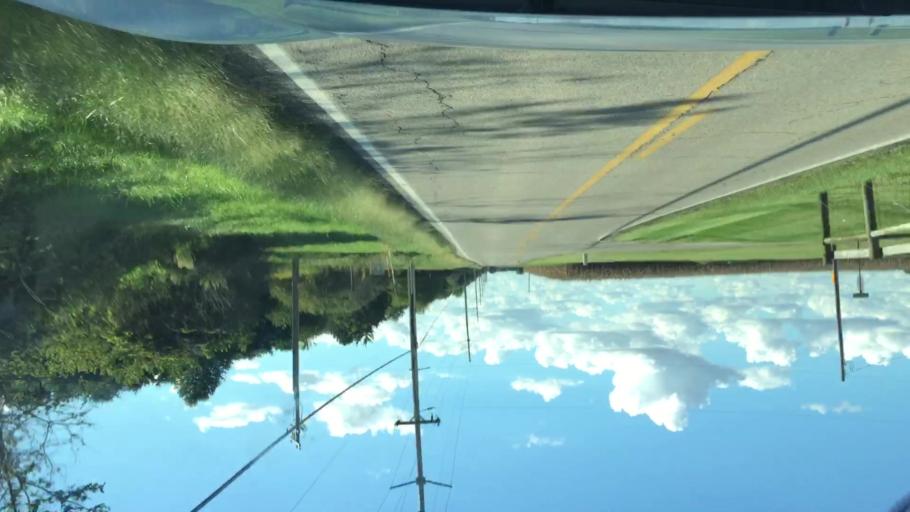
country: US
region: Ohio
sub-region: Clark County
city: Northridge
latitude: 39.9621
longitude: -83.7081
